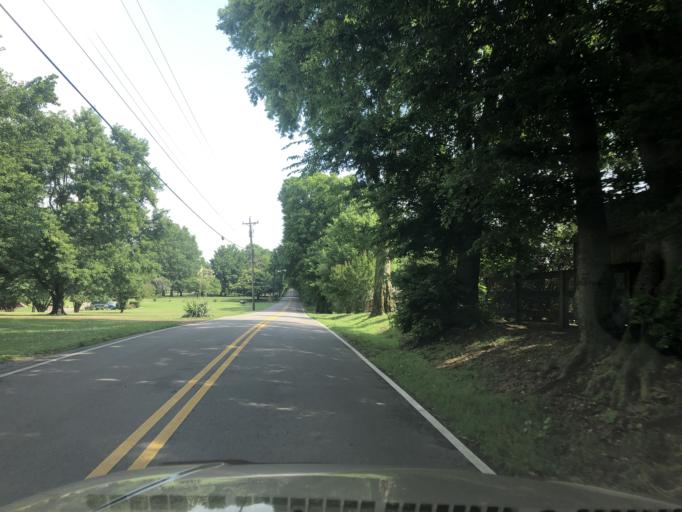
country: US
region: Tennessee
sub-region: Davidson County
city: Lakewood
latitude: 36.2332
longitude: -86.5941
